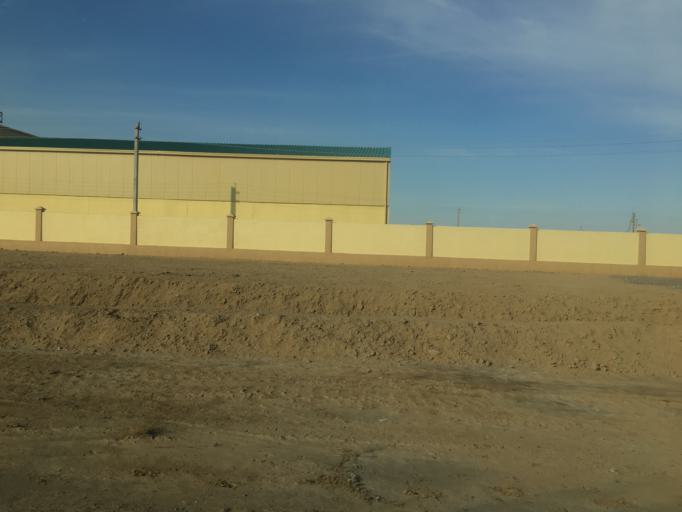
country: TM
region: Mary
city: Mary
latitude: 37.6024
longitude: 61.6286
